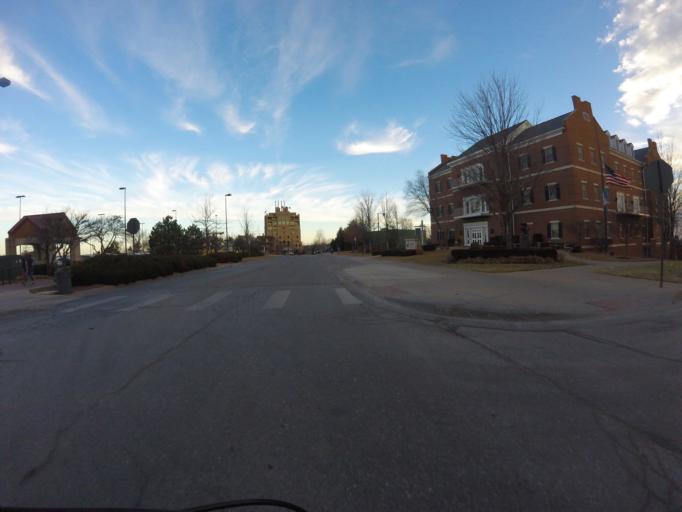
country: US
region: Kansas
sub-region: Douglas County
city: Lawrence
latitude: 38.9531
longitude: -95.2607
